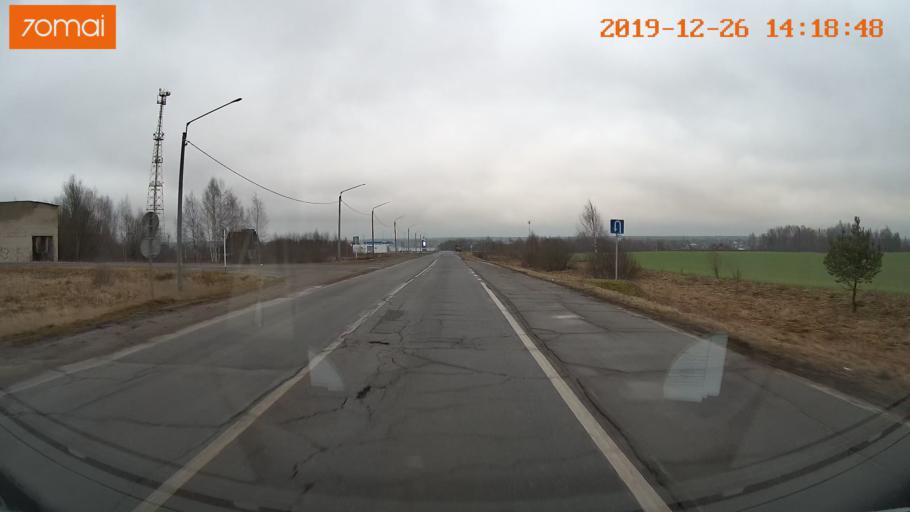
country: RU
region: Jaroslavl
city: Poshekhon'ye
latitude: 58.5134
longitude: 39.1043
